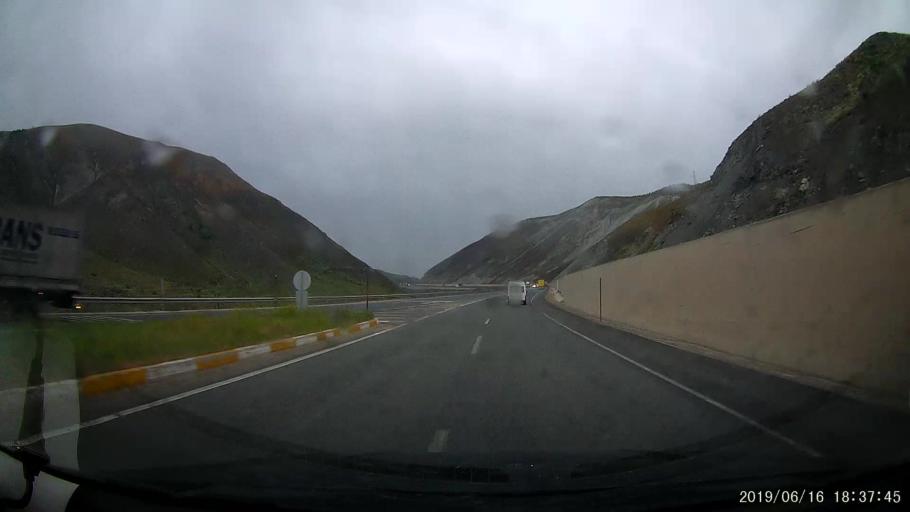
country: TR
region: Erzincan
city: Catalarmut
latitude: 39.8846
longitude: 39.1935
